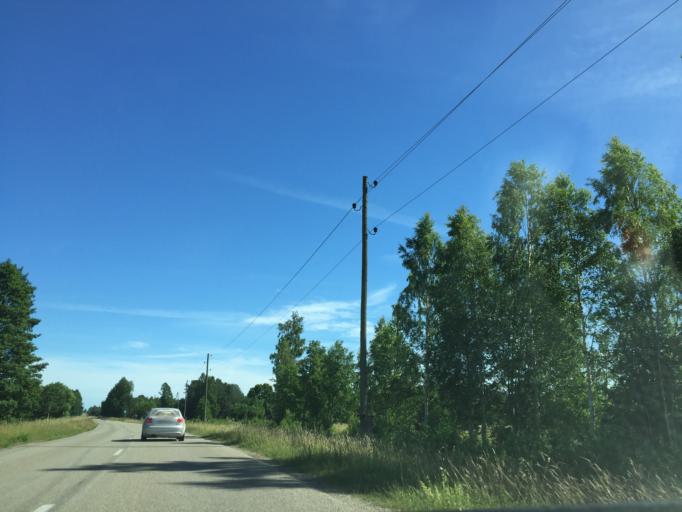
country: LV
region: Rojas
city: Roja
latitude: 57.4641
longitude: 22.8747
